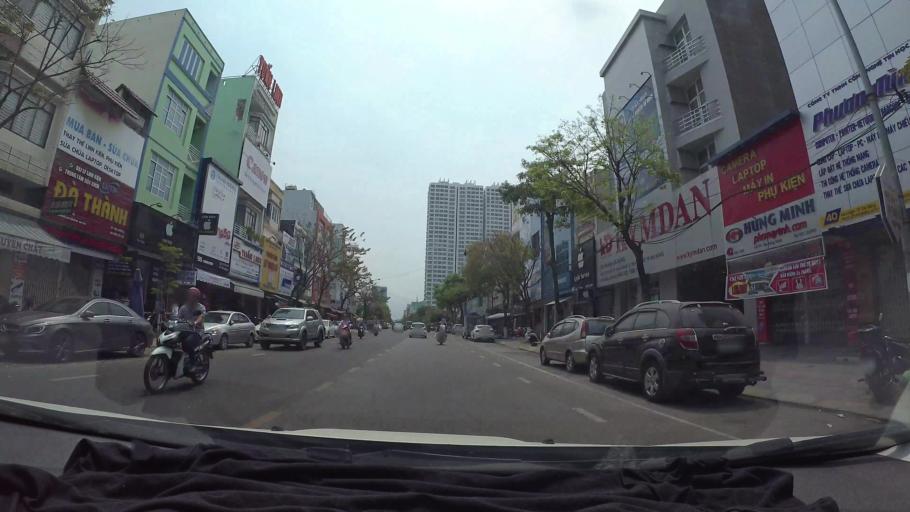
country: VN
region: Da Nang
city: Da Nang
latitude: 16.0653
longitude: 108.2103
